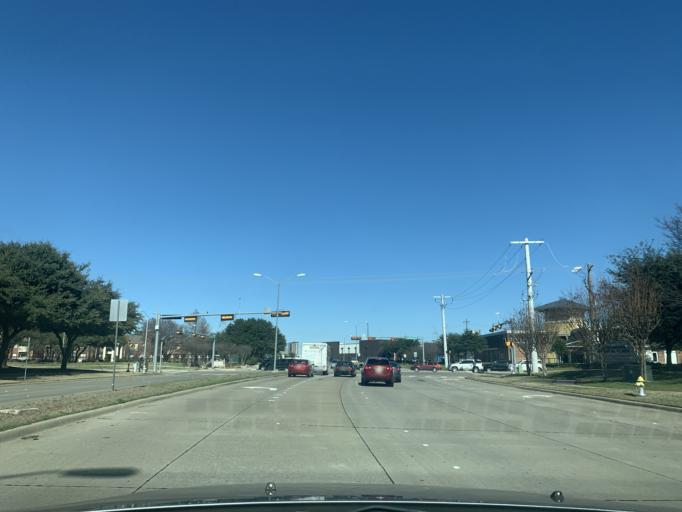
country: US
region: Texas
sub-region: Denton County
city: The Colony
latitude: 33.0551
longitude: -96.8339
